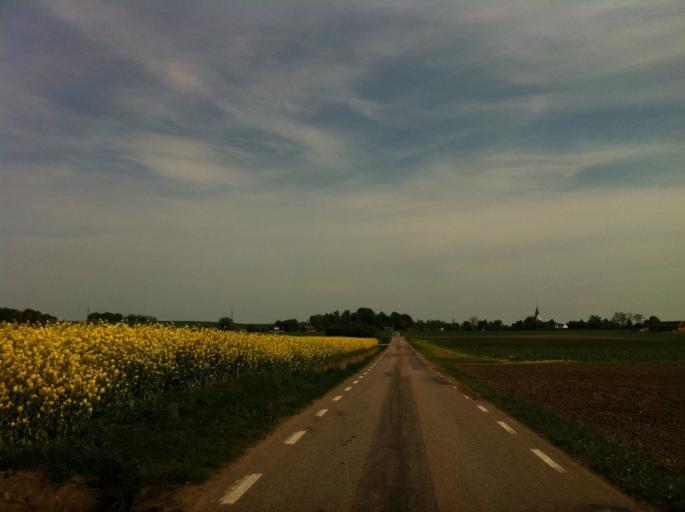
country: SE
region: Skane
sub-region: Landskrona
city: Asmundtorp
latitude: 55.9100
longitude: 12.8897
